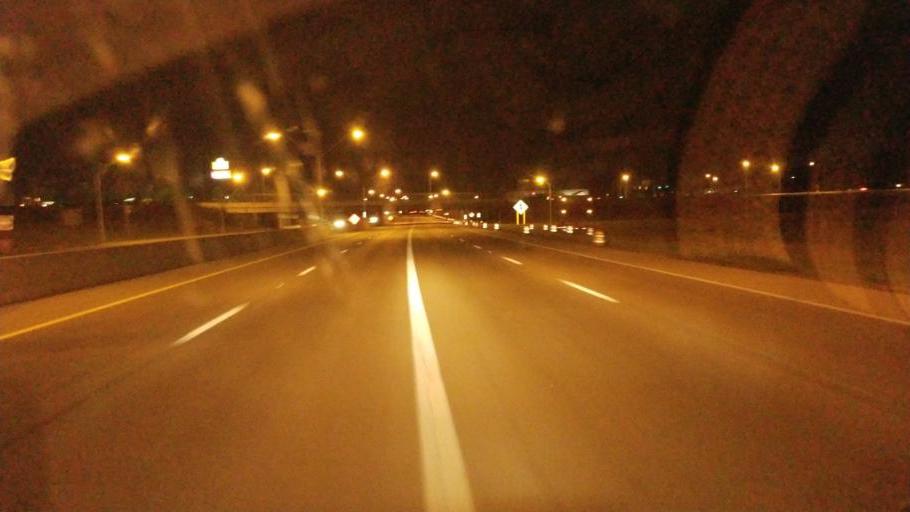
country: US
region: Ohio
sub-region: Franklin County
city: Lincoln Village
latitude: 39.9746
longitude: -83.0973
